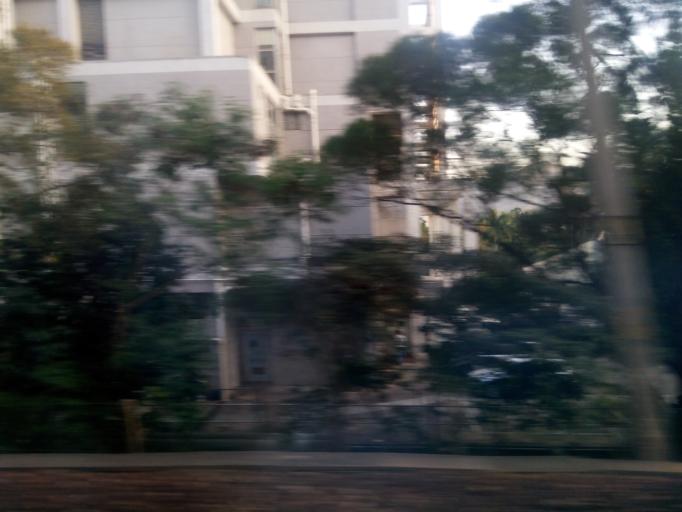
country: HK
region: Sha Tin
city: Sha Tin
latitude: 22.4161
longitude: 114.2122
